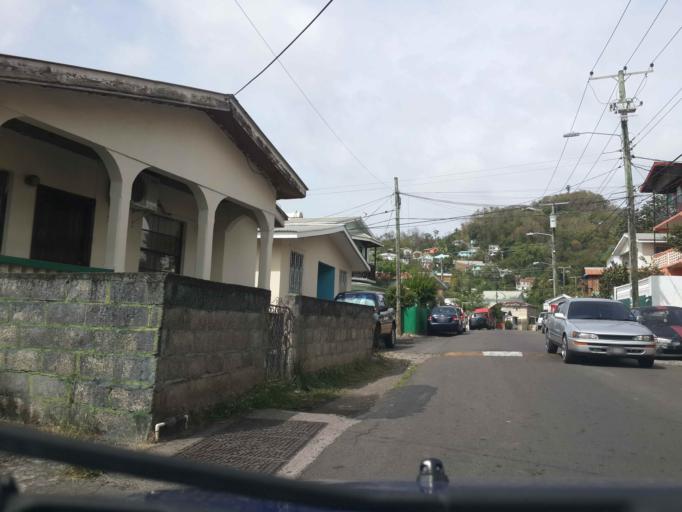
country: LC
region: Castries Quarter
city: Bisee
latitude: 14.0183
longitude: -60.9823
